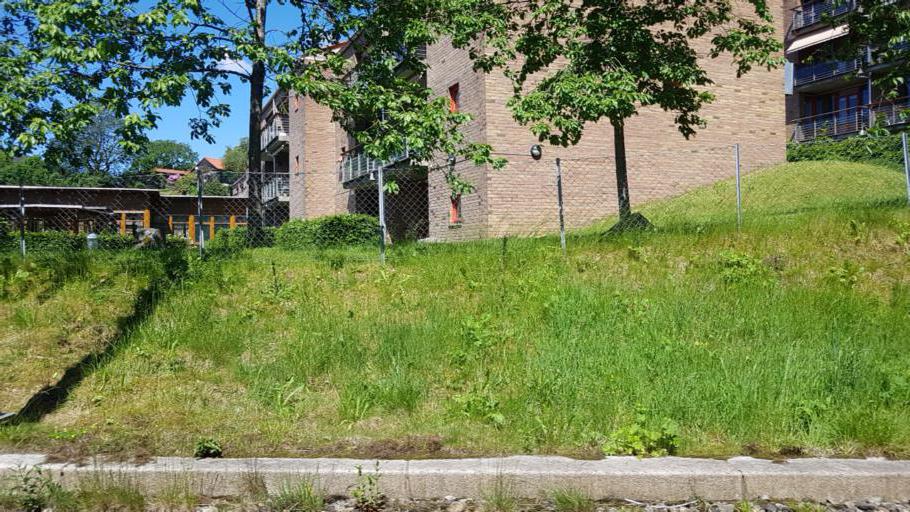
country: NO
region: Hordaland
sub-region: Bergen
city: Bergen
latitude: 60.3470
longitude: 5.3540
